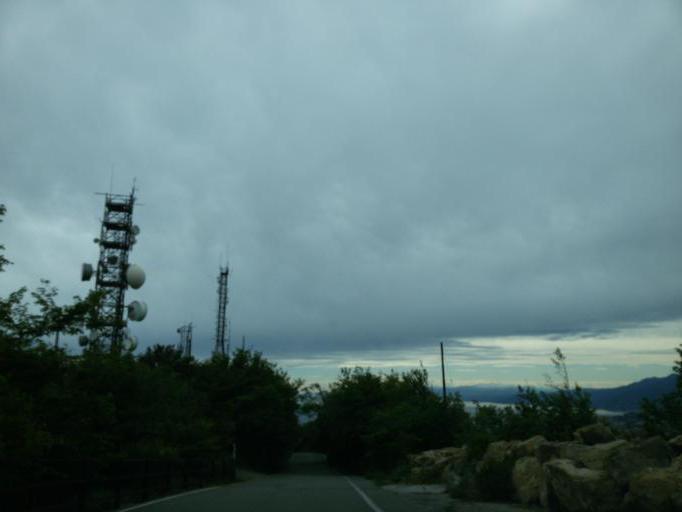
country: IT
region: Liguria
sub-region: Provincia di Genova
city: Genoa
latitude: 44.4349
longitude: 8.9159
